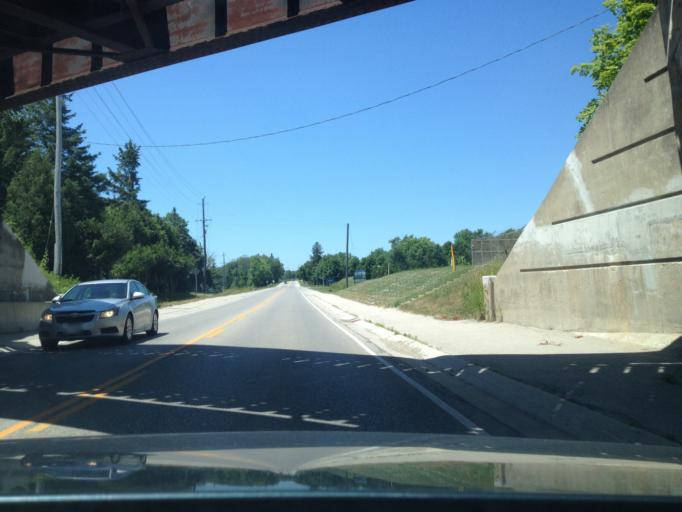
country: CA
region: Ontario
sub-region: Wellington County
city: Guelph
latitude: 43.6909
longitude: -80.3963
